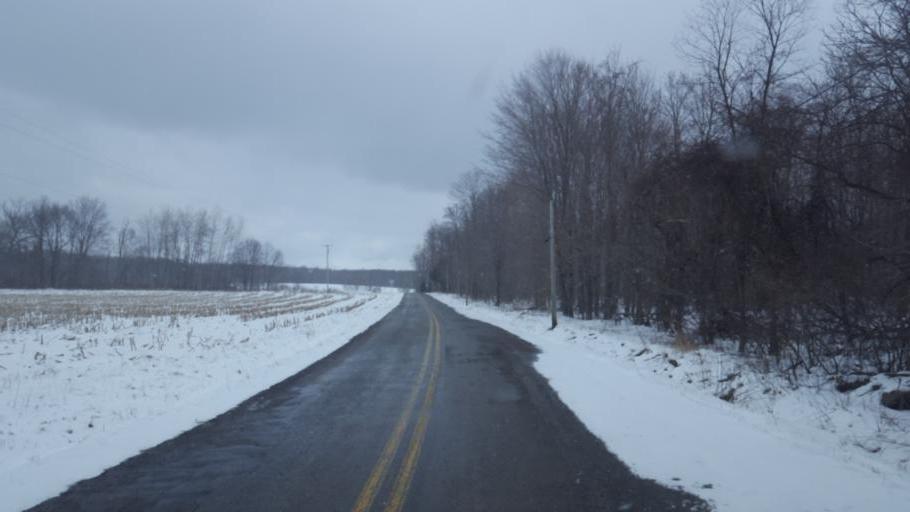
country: US
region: Pennsylvania
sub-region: Crawford County
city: Cochranton
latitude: 41.4277
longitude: -80.0181
